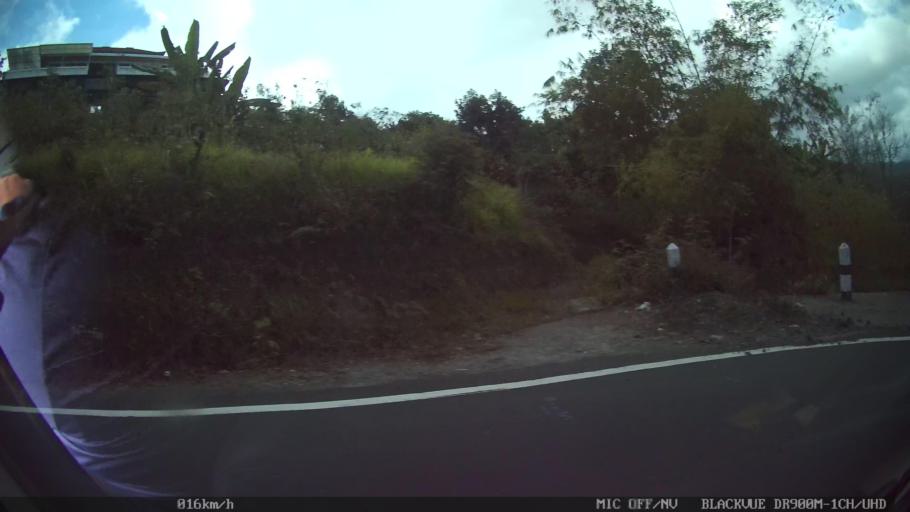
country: ID
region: Bali
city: Banjar Kedisan
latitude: -8.2593
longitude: 115.3416
